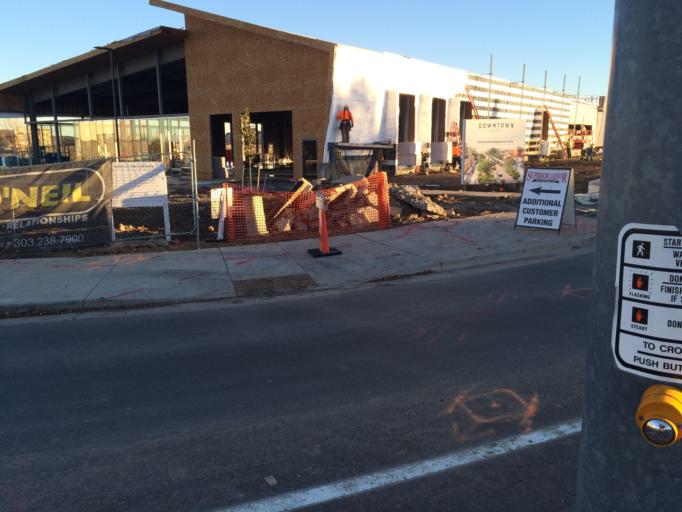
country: US
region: Colorado
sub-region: Boulder County
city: Superior
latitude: 39.9552
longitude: -105.1655
